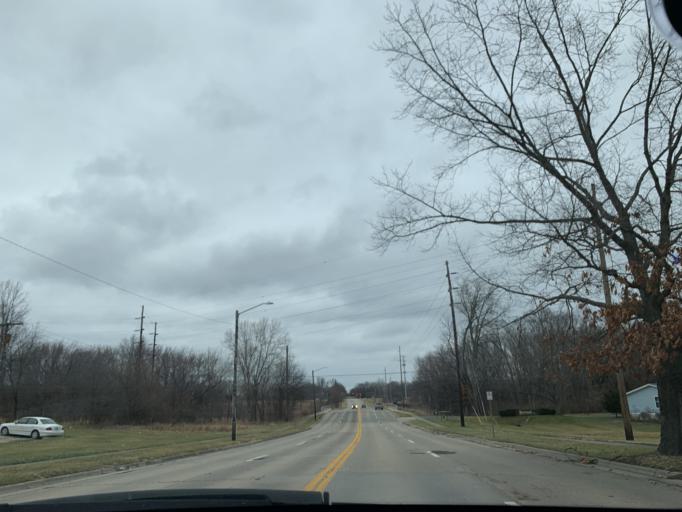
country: US
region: Illinois
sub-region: Sangamon County
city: Leland Grove
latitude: 39.8196
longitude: -89.6872
